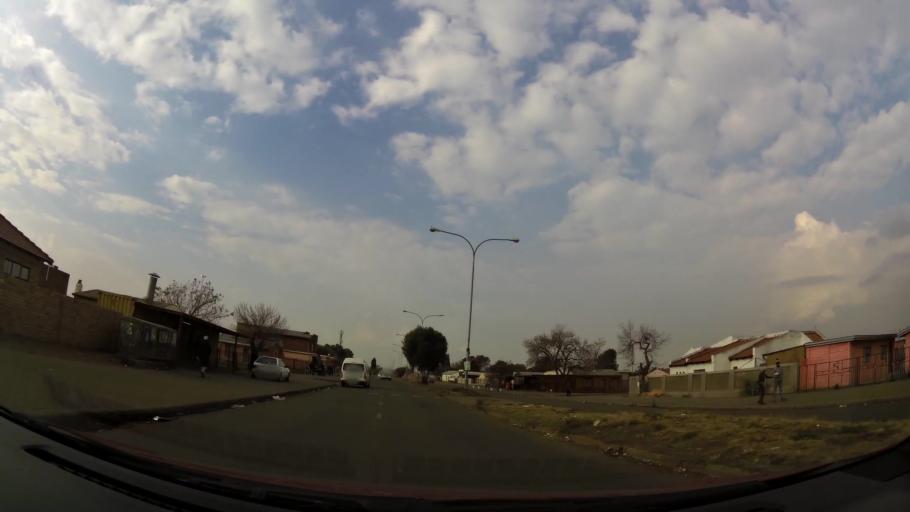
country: ZA
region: Gauteng
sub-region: Sedibeng District Municipality
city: Vanderbijlpark
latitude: -26.6839
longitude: 27.8764
